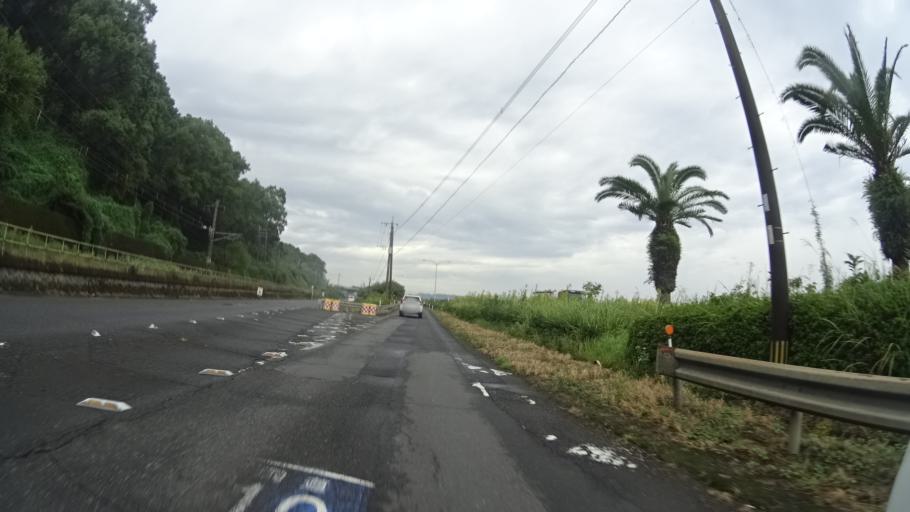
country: JP
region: Kagoshima
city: Kajiki
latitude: 31.6949
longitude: 130.6142
